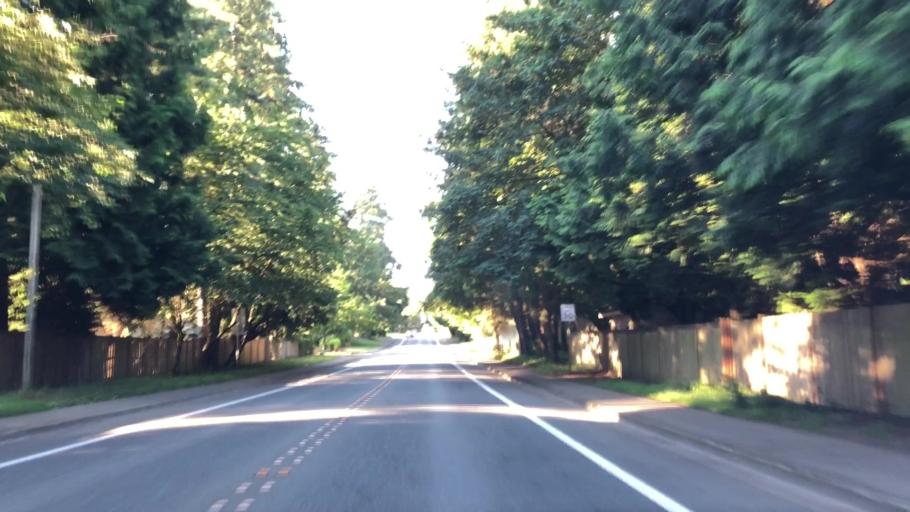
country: US
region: Washington
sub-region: King County
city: Redmond
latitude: 47.6978
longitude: -122.1192
